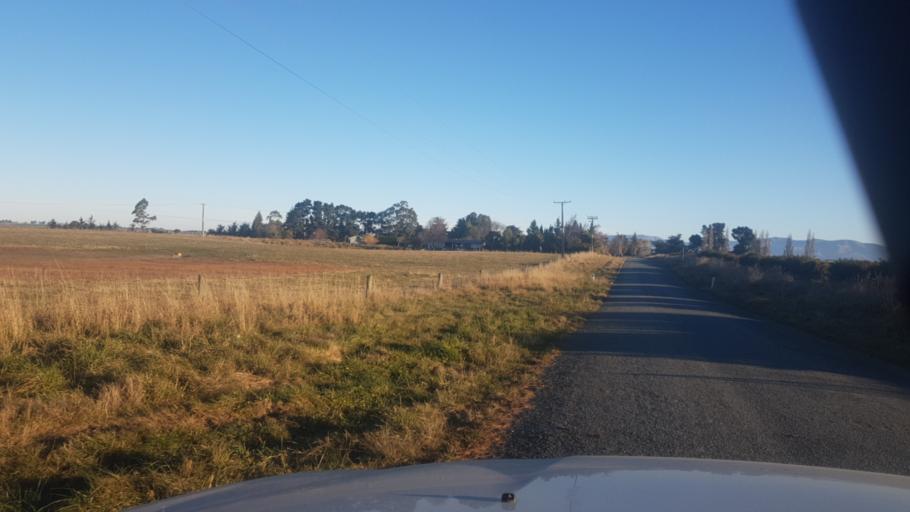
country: NZ
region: Canterbury
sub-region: Timaru District
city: Timaru
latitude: -44.4601
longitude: 171.1600
